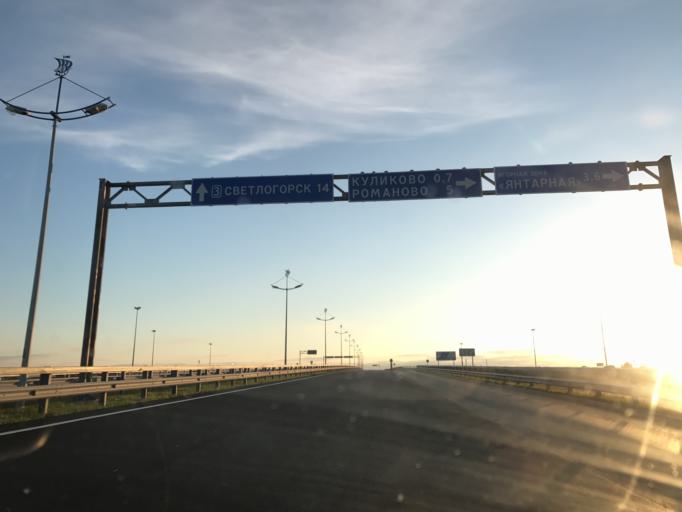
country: RU
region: Kaliningrad
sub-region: Gorod Kaliningrad
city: Pionerskiy
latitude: 54.9214
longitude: 20.3334
